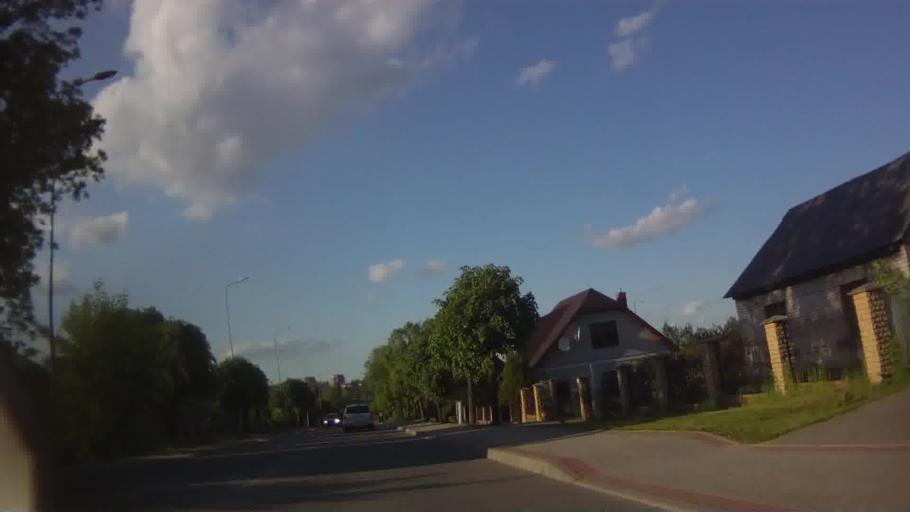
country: LV
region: Rezekne
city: Rezekne
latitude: 56.5138
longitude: 27.3419
